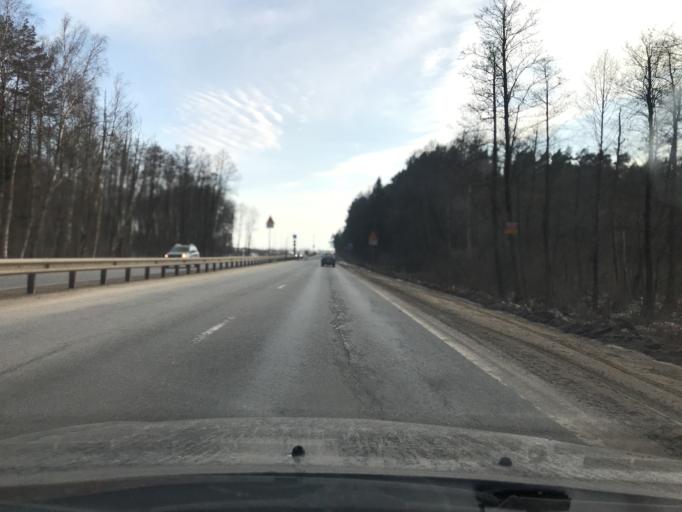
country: RU
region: Kaluga
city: Kaluga
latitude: 54.4505
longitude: 36.2350
